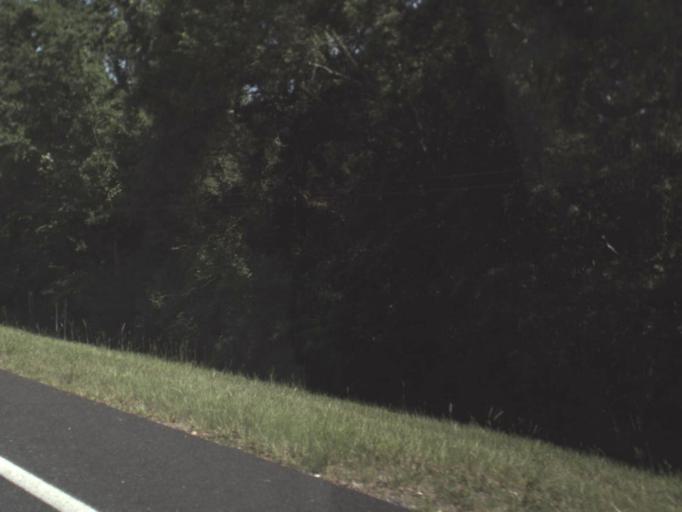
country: US
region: Florida
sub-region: Levy County
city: Manatee Road
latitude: 29.5930
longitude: -82.9652
